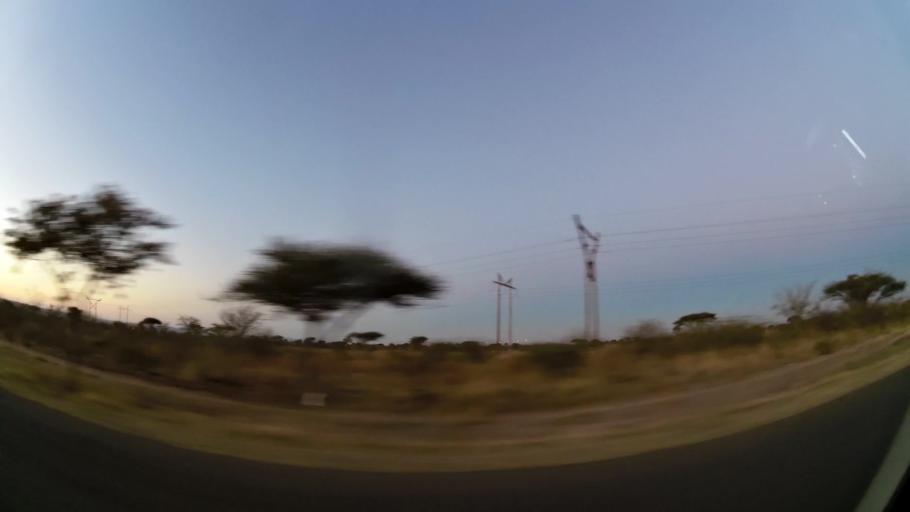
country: ZA
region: Limpopo
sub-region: Capricorn District Municipality
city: Polokwane
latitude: -23.8618
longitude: 29.4061
